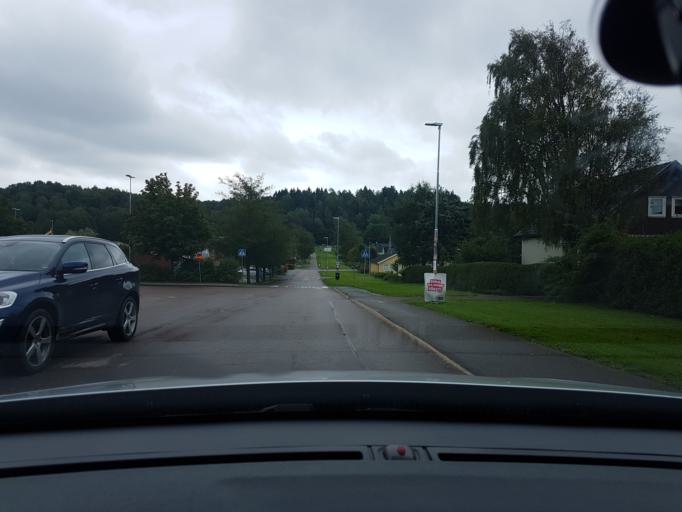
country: SE
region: Vaestra Goetaland
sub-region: Ale Kommun
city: Salanda
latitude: 57.9836
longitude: 12.2104
